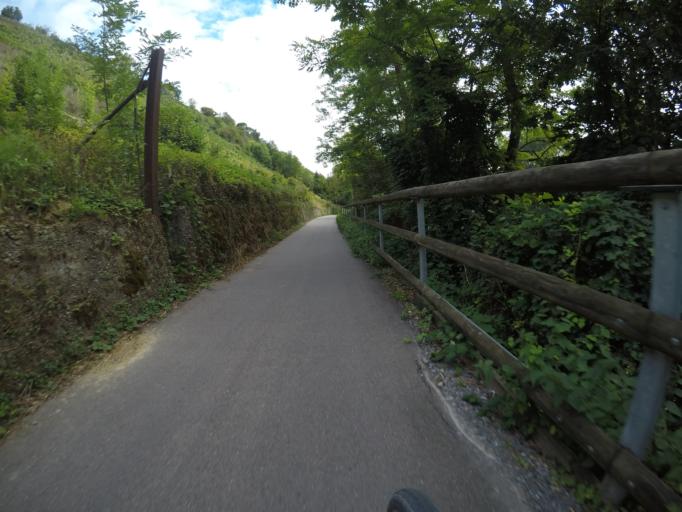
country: DE
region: Baden-Wuerttemberg
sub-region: Regierungsbezirk Stuttgart
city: Freiberg am Neckar
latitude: 48.9265
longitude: 9.2178
